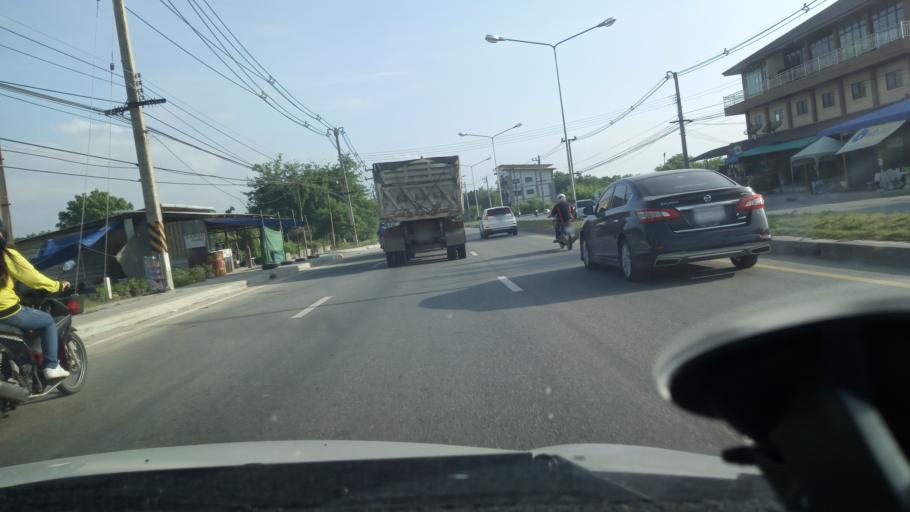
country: TH
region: Chon Buri
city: Phan Thong
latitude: 13.4280
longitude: 101.1091
